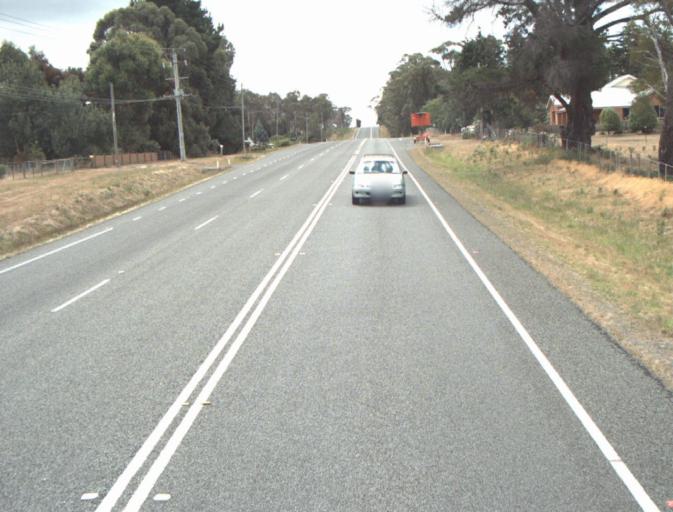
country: AU
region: Tasmania
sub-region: Launceston
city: Mayfield
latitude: -41.2851
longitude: 147.0401
